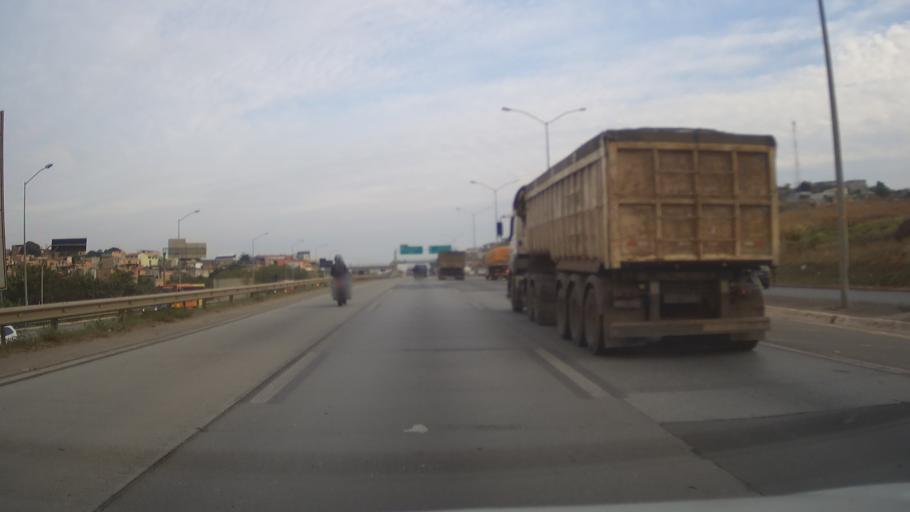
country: BR
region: Minas Gerais
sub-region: Vespasiano
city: Vespasiano
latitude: -19.7752
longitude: -43.9486
